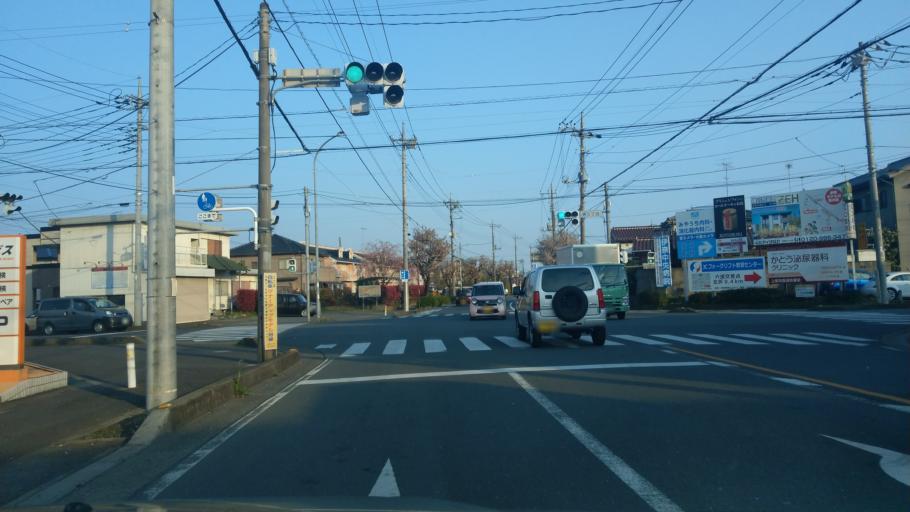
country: JP
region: Saitama
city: Ageoshimo
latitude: 36.0071
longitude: 139.6045
